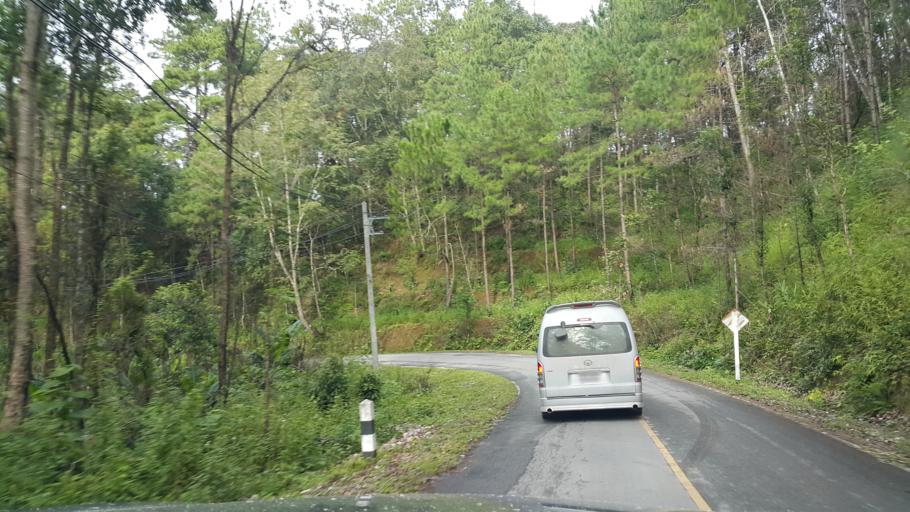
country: TH
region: Chiang Mai
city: Chaem Luang
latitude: 18.9305
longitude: 98.4785
